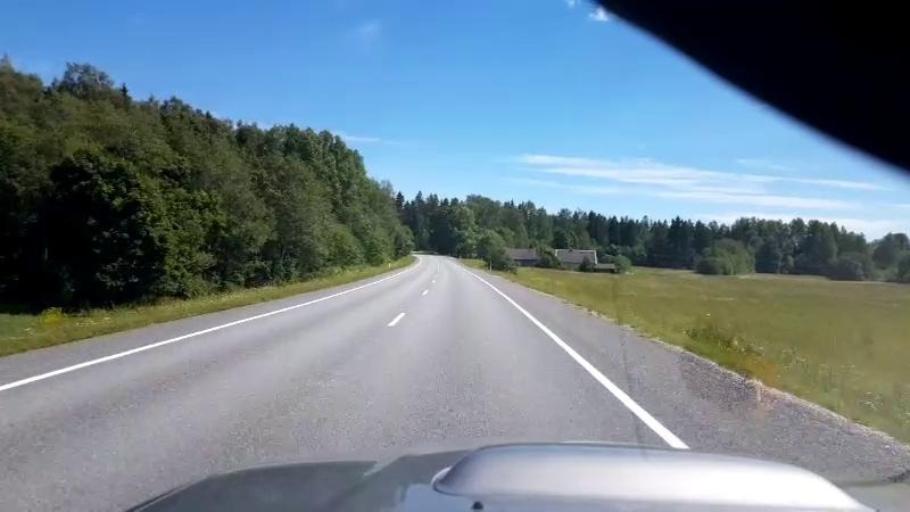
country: EE
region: Jaervamaa
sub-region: Jaerva-Jaani vald
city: Jarva-Jaani
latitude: 58.9982
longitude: 25.9416
